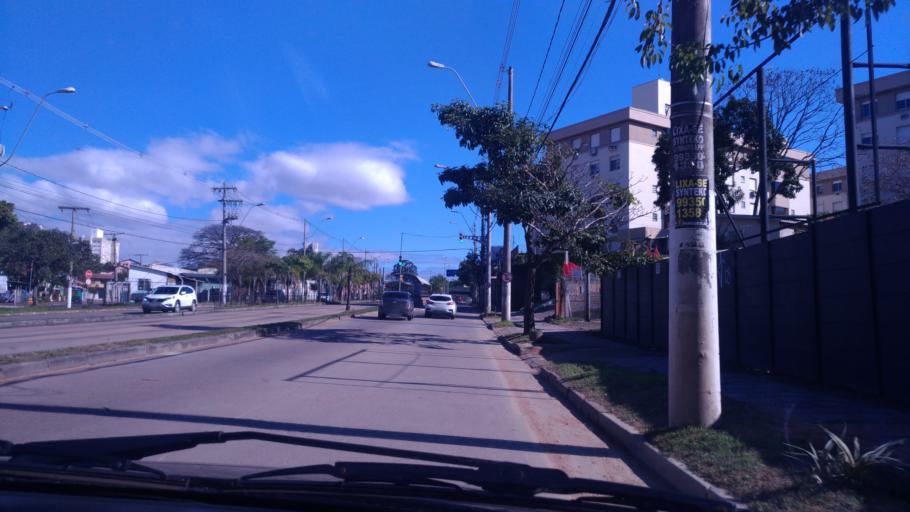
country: BR
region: Rio Grande do Sul
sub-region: Porto Alegre
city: Porto Alegre
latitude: -30.0758
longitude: -51.2057
